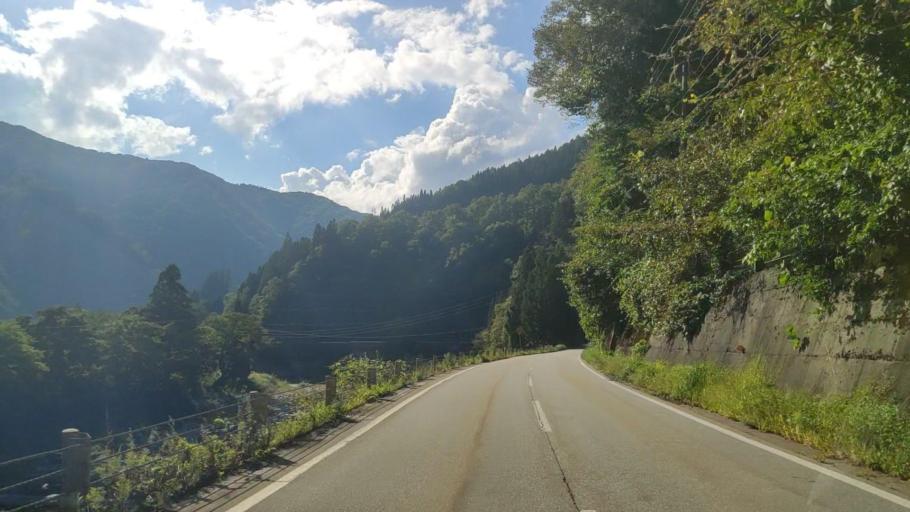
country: JP
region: Gifu
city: Takayama
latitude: 36.2975
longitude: 137.1263
